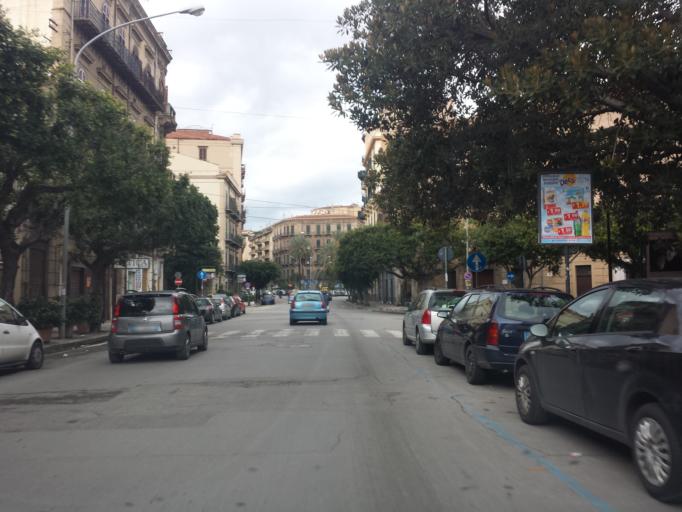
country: IT
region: Sicily
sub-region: Palermo
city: Palermo
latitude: 38.1213
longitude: 13.3524
